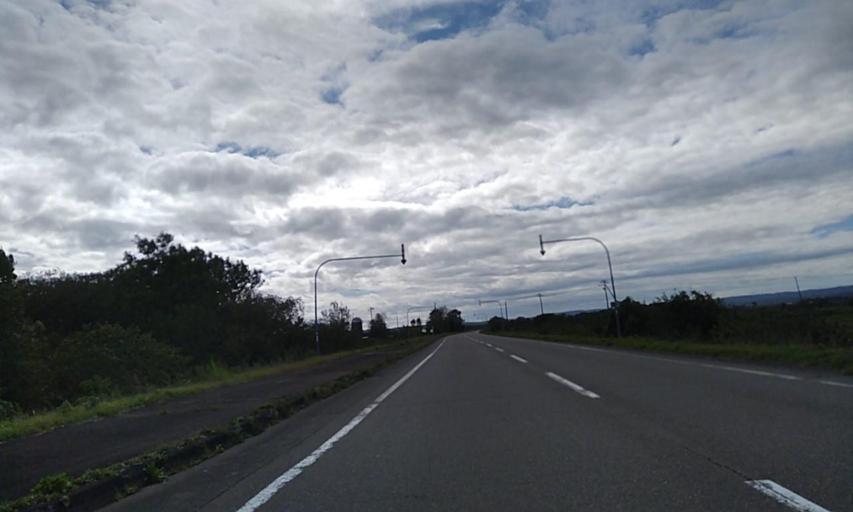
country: JP
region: Hokkaido
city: Obihiro
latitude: 42.7219
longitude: 143.6583
